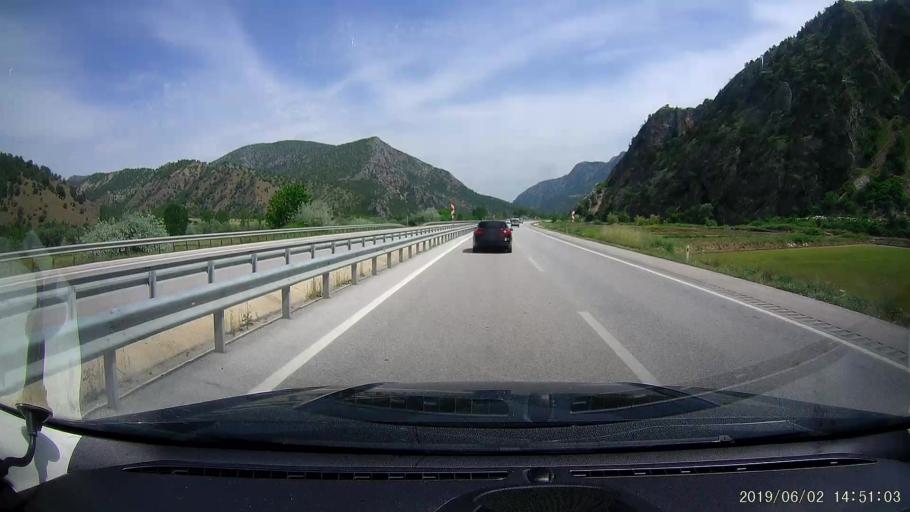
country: TR
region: Corum
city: Kargi
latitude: 41.0658
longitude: 34.5332
